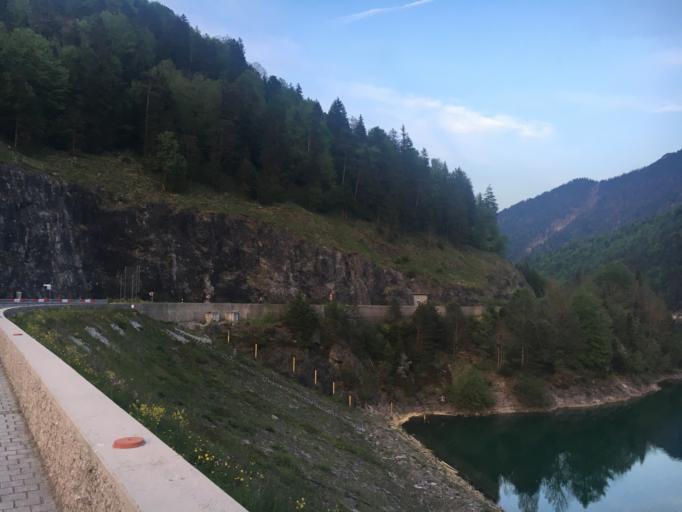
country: DE
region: Bavaria
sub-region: Upper Bavaria
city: Lenggries
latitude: 47.5864
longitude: 11.5499
